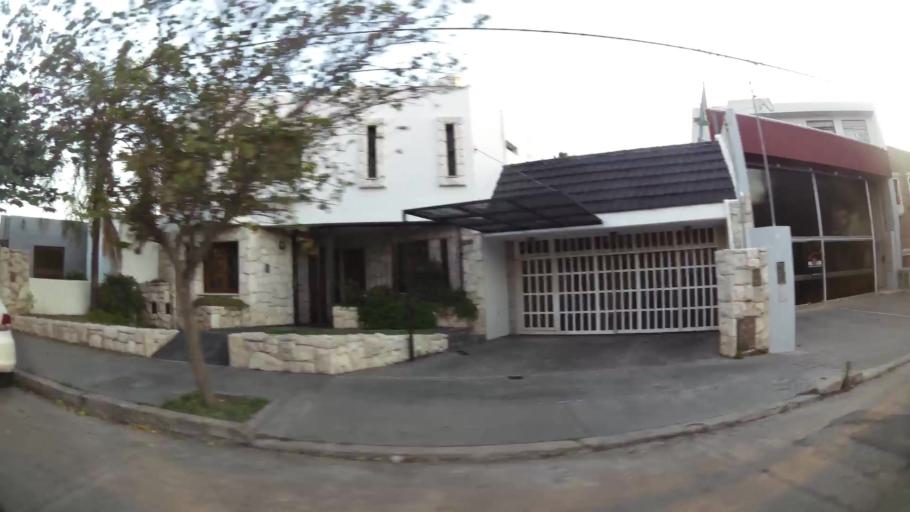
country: AR
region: Cordoba
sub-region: Departamento de Capital
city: Cordoba
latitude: -31.3825
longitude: -64.2182
